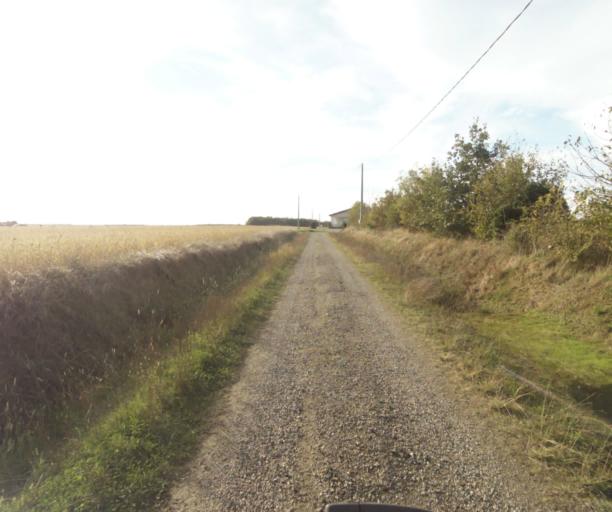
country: FR
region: Midi-Pyrenees
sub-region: Departement du Tarn-et-Garonne
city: Finhan
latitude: 43.9115
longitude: 1.1303
